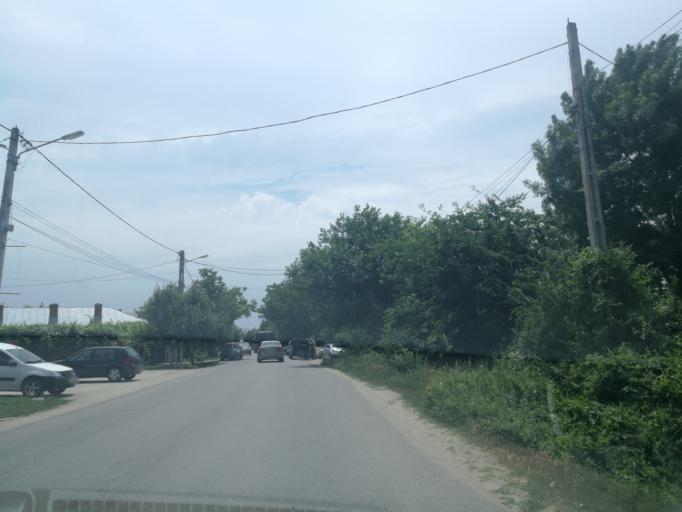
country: RO
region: Ilfov
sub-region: Comuna Vidra
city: Cretesti
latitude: 44.2818
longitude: 26.1338
